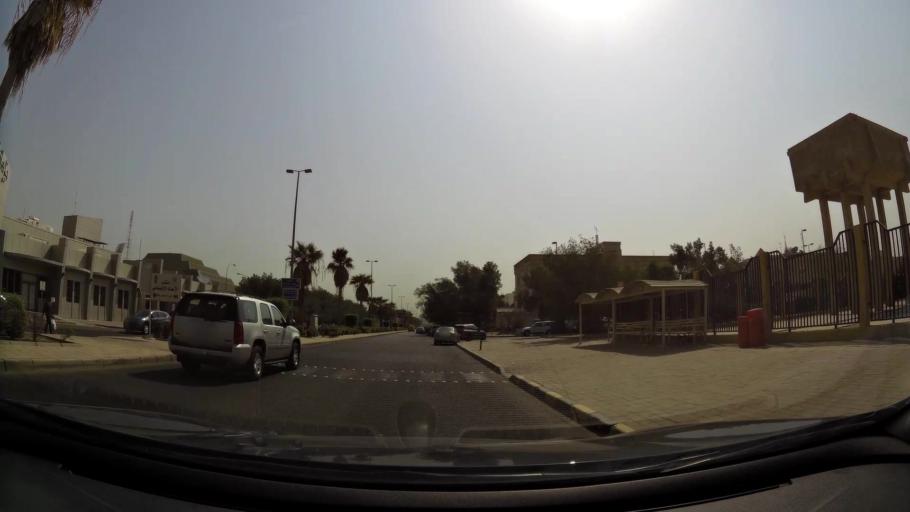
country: KW
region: Al Asimah
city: Ad Dasmah
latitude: 29.3589
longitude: 47.9963
